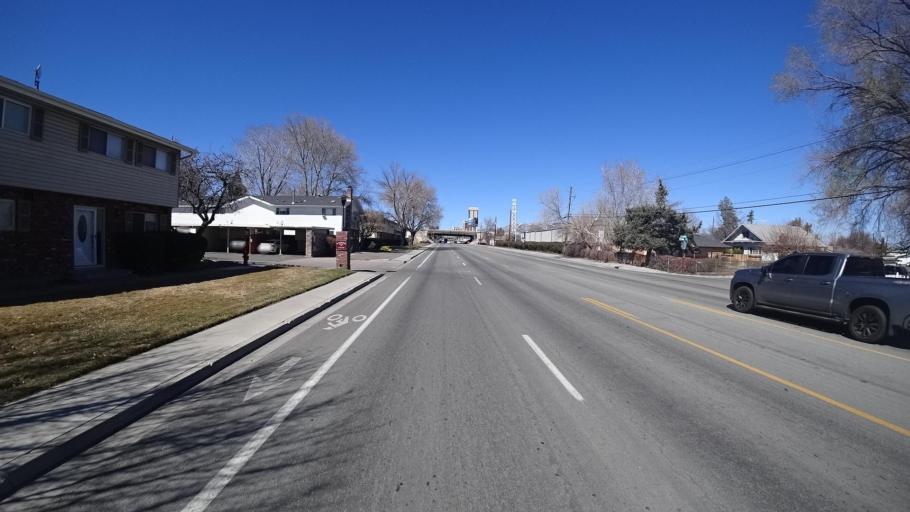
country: US
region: Nevada
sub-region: Washoe County
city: Reno
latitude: 39.4848
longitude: -119.7832
